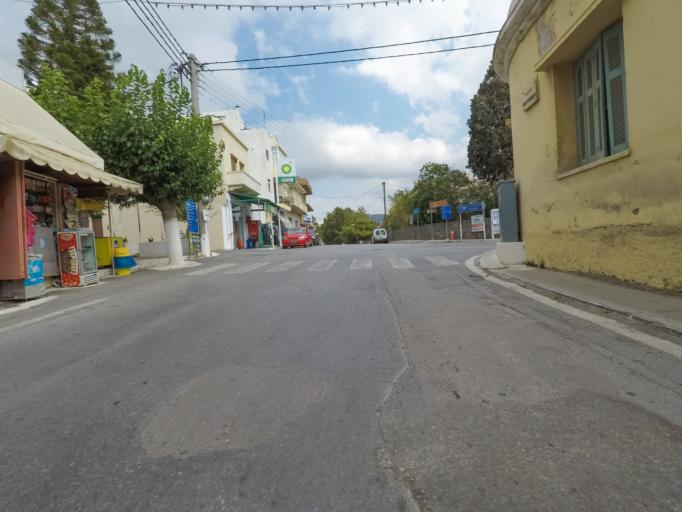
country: GR
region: Crete
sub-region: Nomos Lasithiou
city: Neapoli
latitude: 35.2577
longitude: 25.6079
